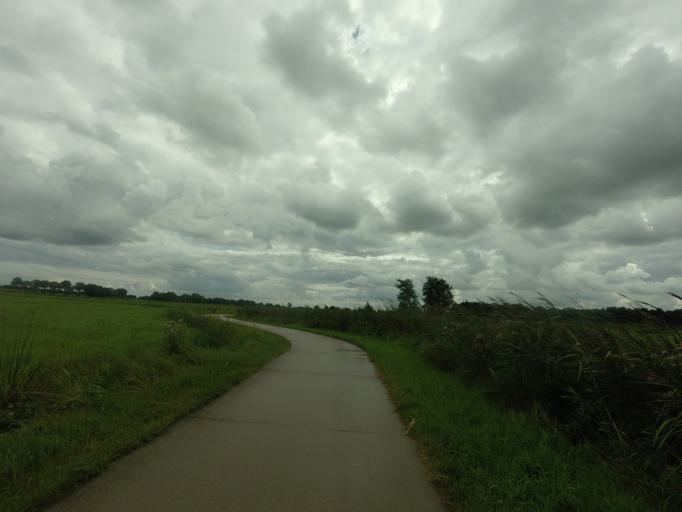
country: NL
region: Overijssel
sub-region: Gemeente Steenwijkerland
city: Wanneperveen
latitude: 52.7177
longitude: 6.1302
